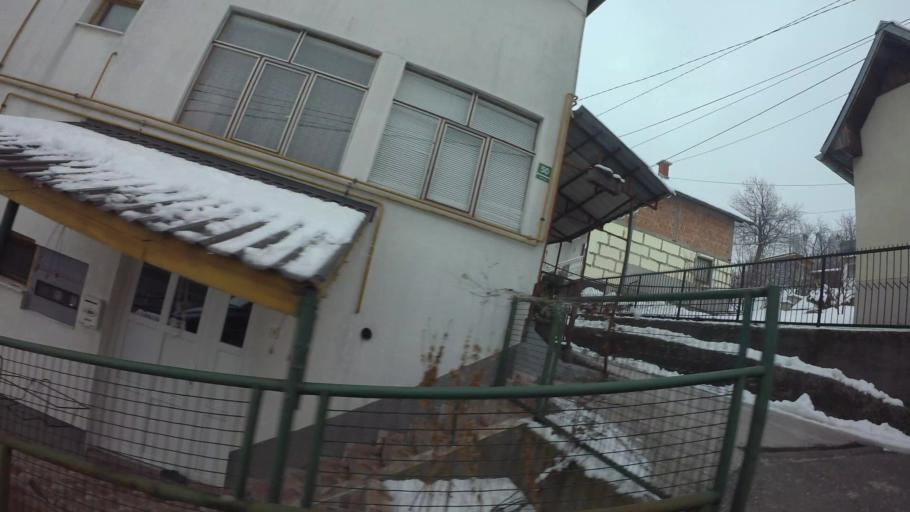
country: BA
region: Federation of Bosnia and Herzegovina
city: Kobilja Glava
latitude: 43.8518
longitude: 18.4190
